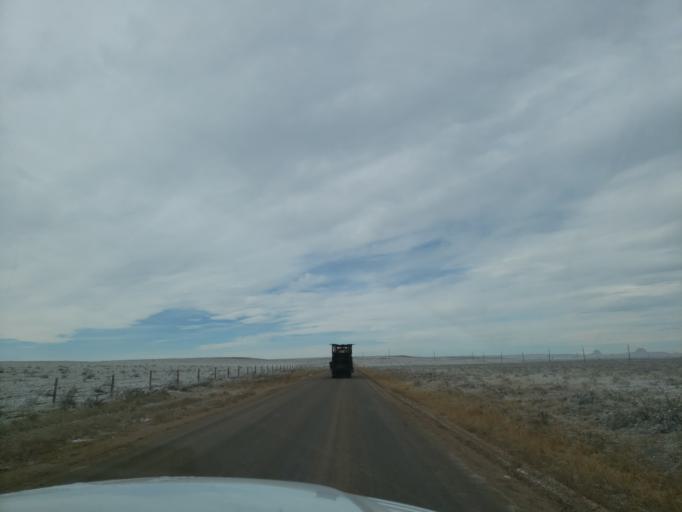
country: US
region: Wyoming
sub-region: Laramie County
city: Pine Bluffs
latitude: 40.7876
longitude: -103.8808
